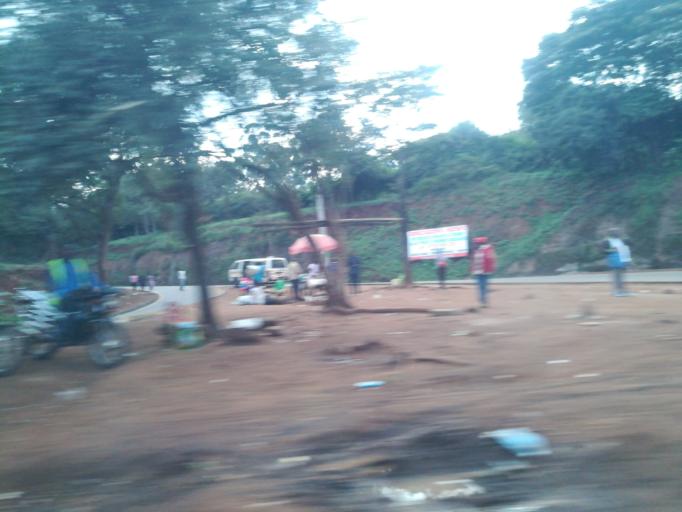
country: KE
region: Nairobi Area
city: Thika
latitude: -1.0244
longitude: 37.0661
